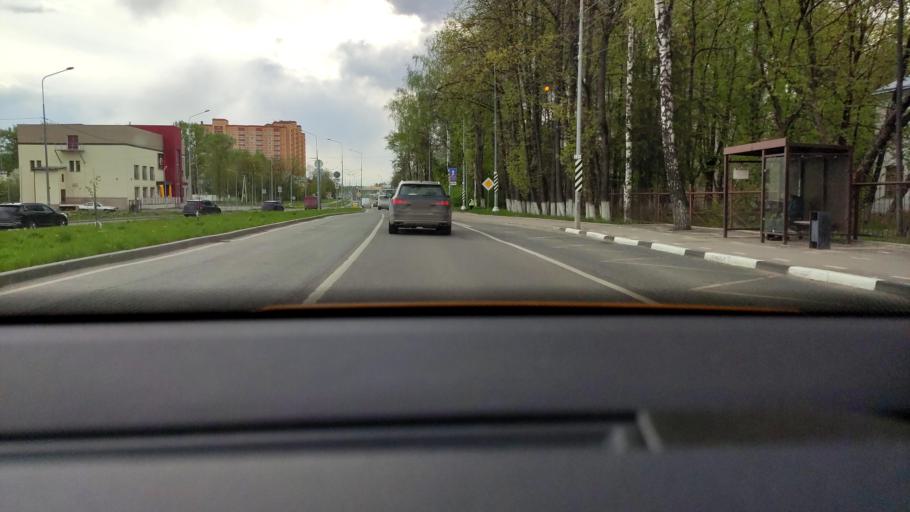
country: RU
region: Moskovskaya
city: Nakhabino
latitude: 55.8422
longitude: 37.1685
